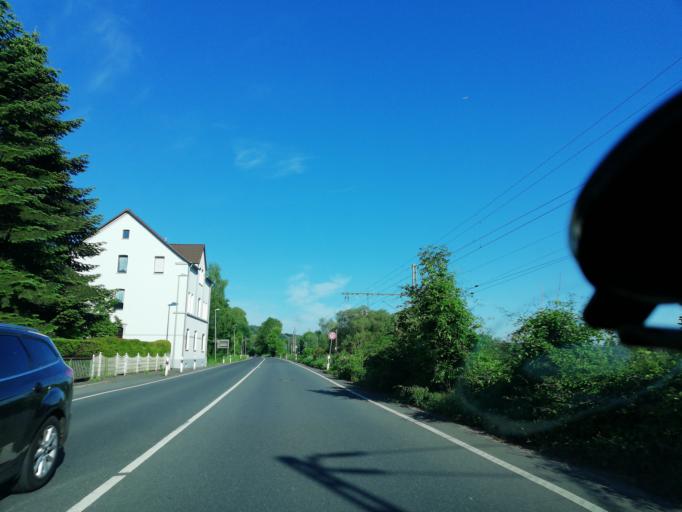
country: DE
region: North Rhine-Westphalia
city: Wetter (Ruhr)
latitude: 51.3911
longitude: 7.3684
